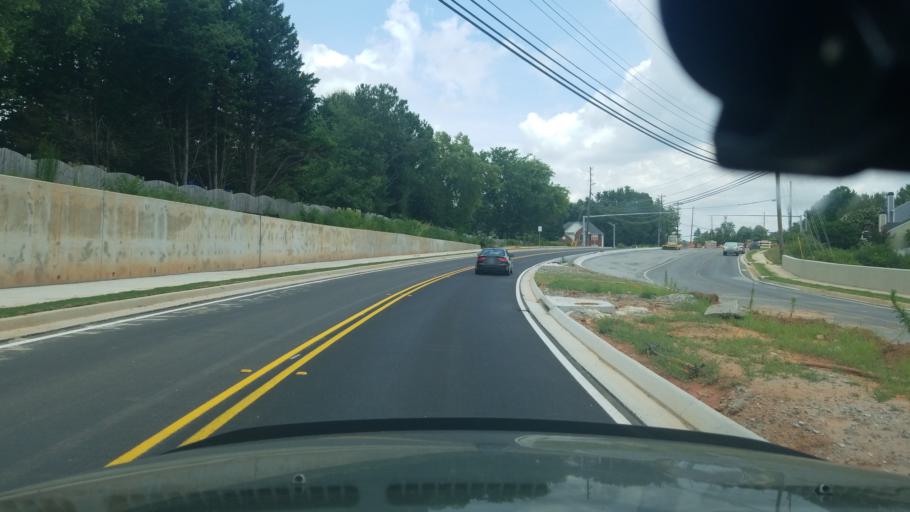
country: US
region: Georgia
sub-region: Fulton County
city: Milton
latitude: 34.1182
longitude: -84.2365
